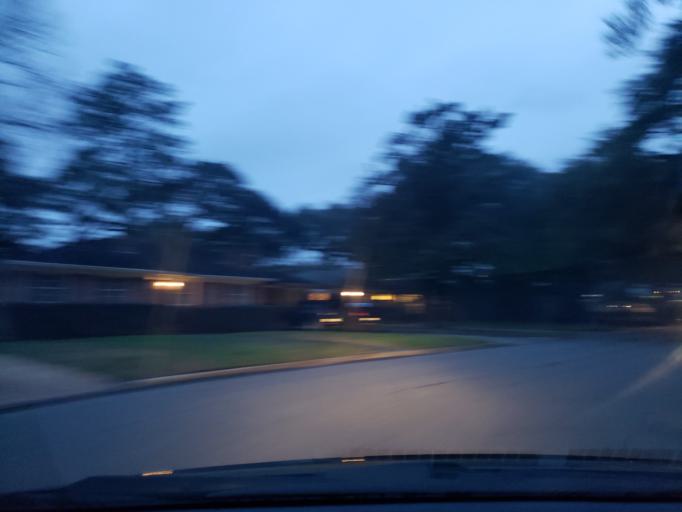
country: US
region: Georgia
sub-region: Chatham County
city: Savannah
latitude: 32.0290
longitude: -81.1067
